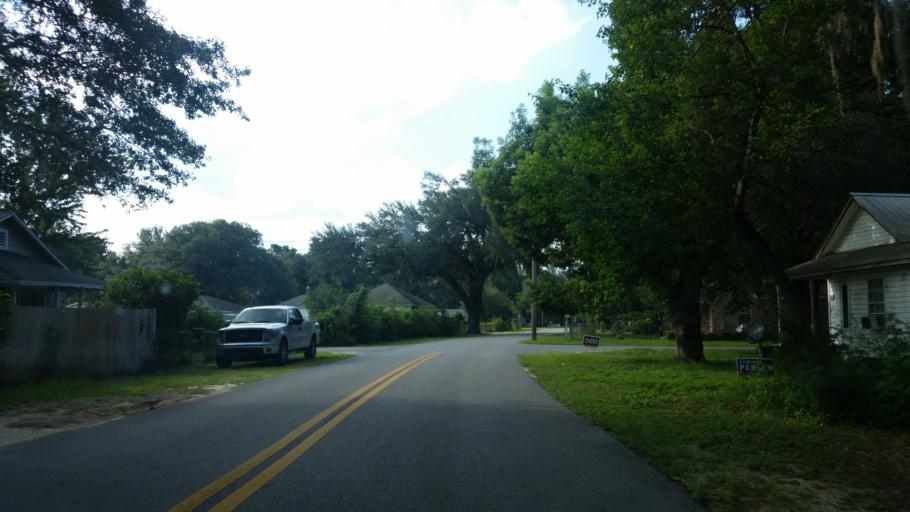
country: US
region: Florida
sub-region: Santa Rosa County
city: Bagdad
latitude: 30.6001
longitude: -87.0335
